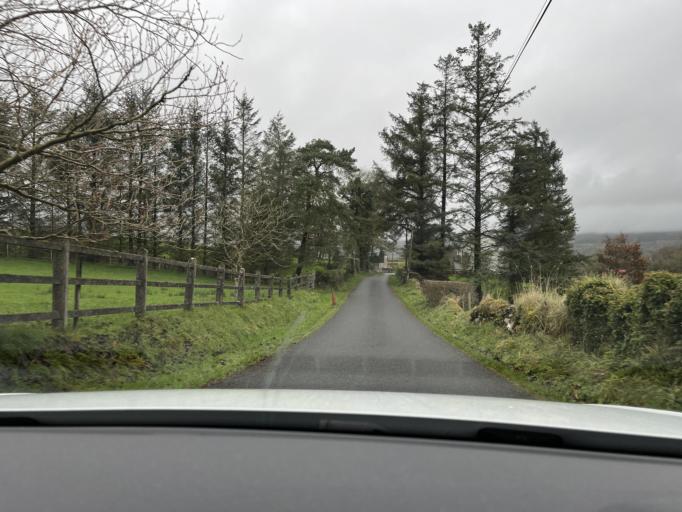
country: IE
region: Connaught
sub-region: County Leitrim
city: Manorhamilton
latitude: 54.2903
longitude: -8.1251
